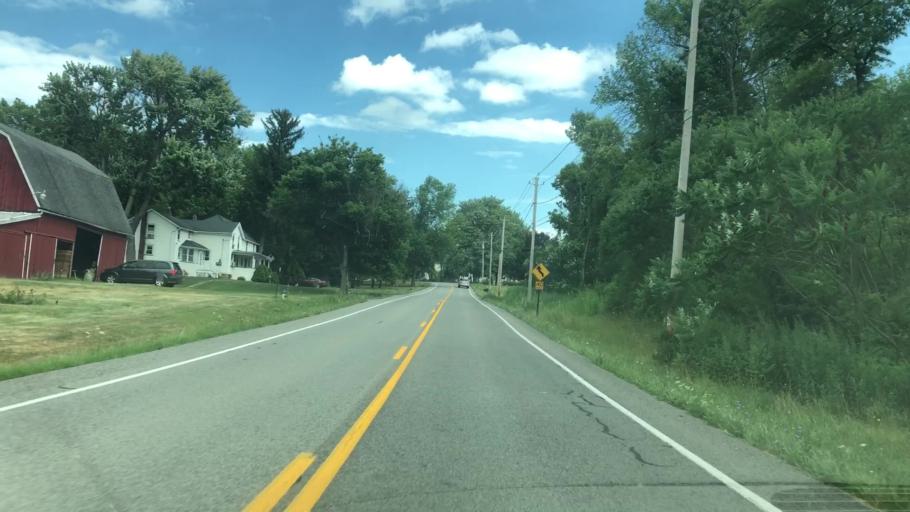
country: US
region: New York
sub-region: Wayne County
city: Macedon
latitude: 43.1212
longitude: -77.3526
